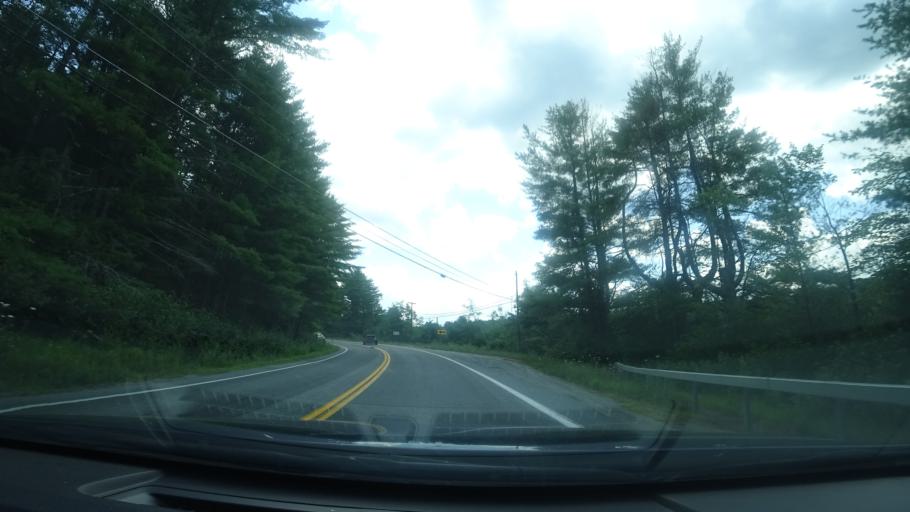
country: US
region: New York
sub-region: Warren County
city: Warrensburg
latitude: 43.6619
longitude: -73.8211
